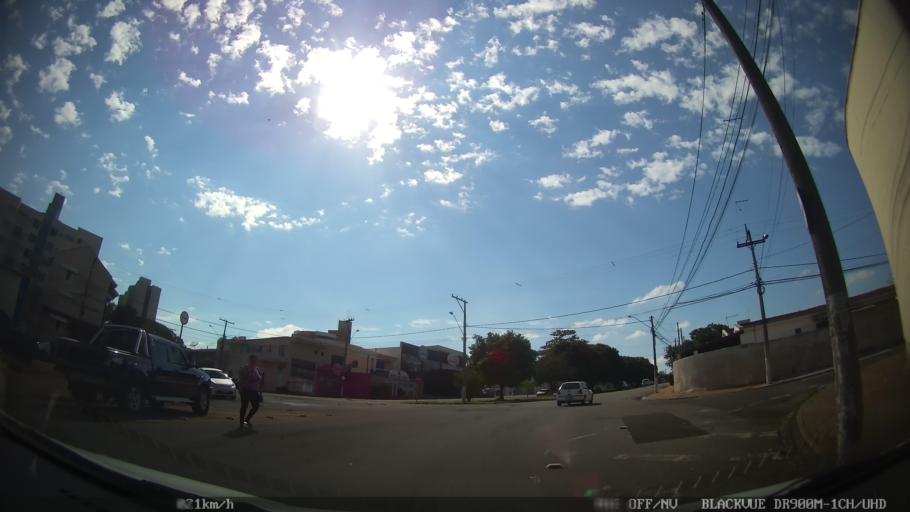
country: BR
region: Sao Paulo
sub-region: Americana
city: Americana
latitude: -22.7411
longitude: -47.3056
